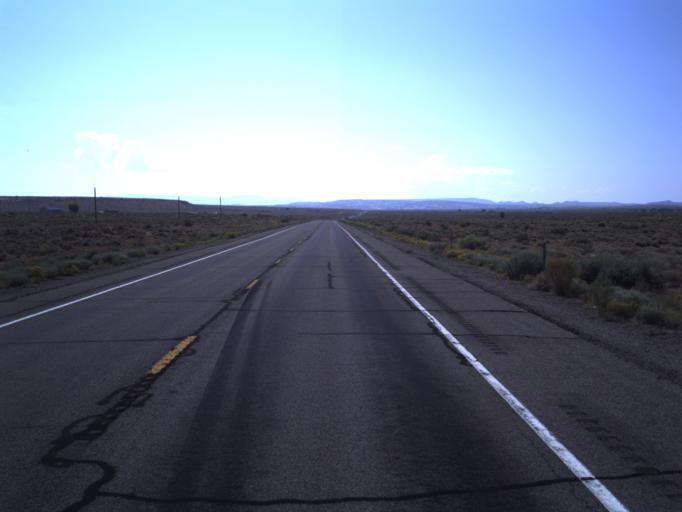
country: US
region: Utah
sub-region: San Juan County
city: Blanding
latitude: 37.1764
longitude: -109.5847
